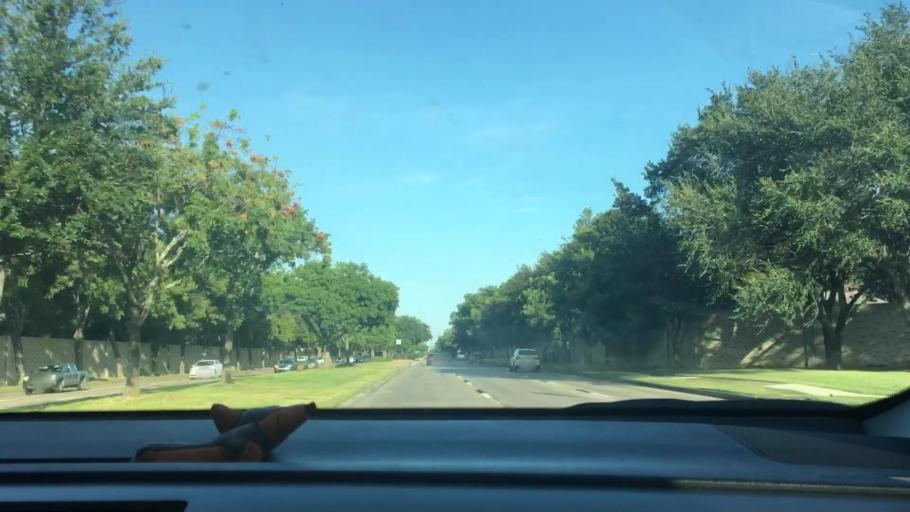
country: US
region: Texas
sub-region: Fort Bend County
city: Sugar Land
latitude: 29.5937
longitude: -95.6097
